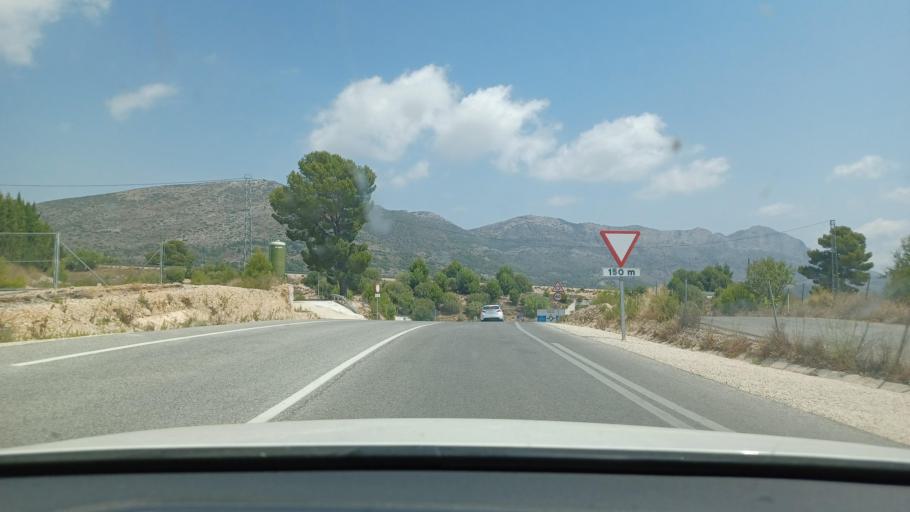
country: ES
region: Valencia
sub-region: Provincia de Alicante
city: Muro del Alcoy
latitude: 38.7924
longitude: -0.4499
